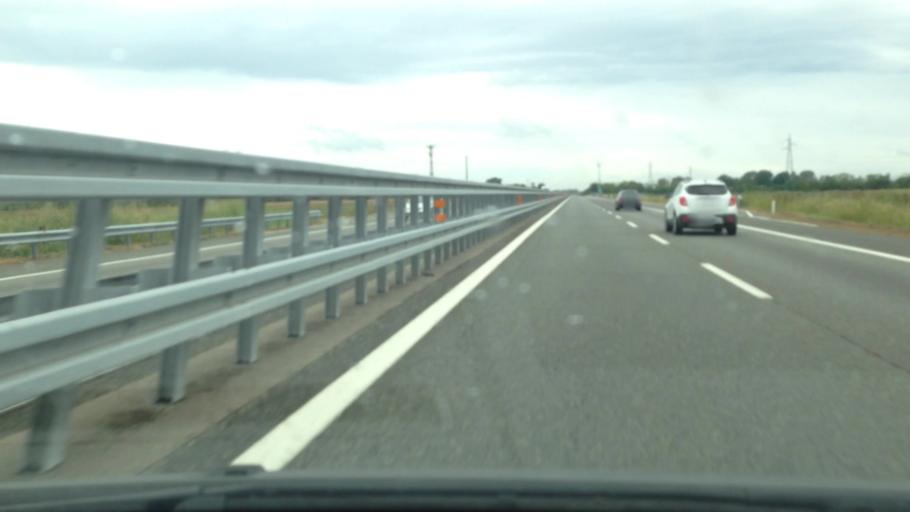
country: IT
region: Piedmont
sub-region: Provincia di Alessandria
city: Solero
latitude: 44.9280
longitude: 8.5158
